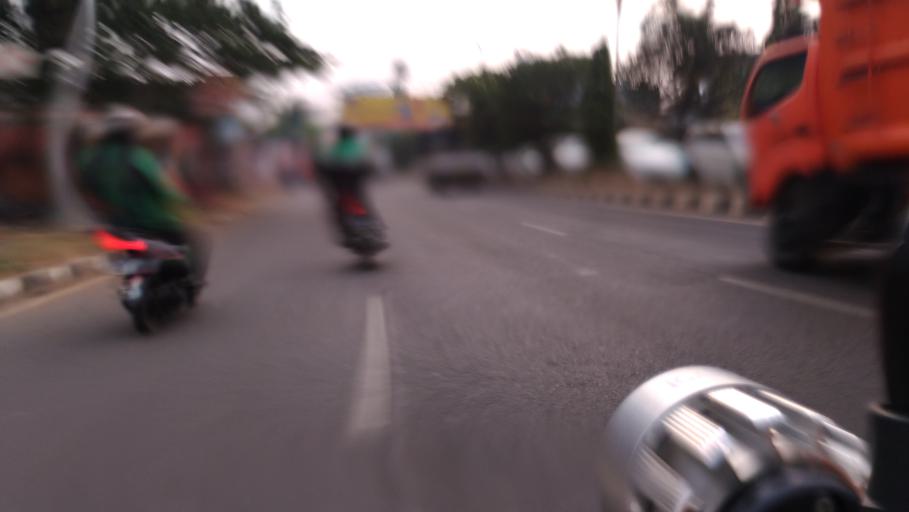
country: ID
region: West Java
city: Cileungsir
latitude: -6.3755
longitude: 106.9104
